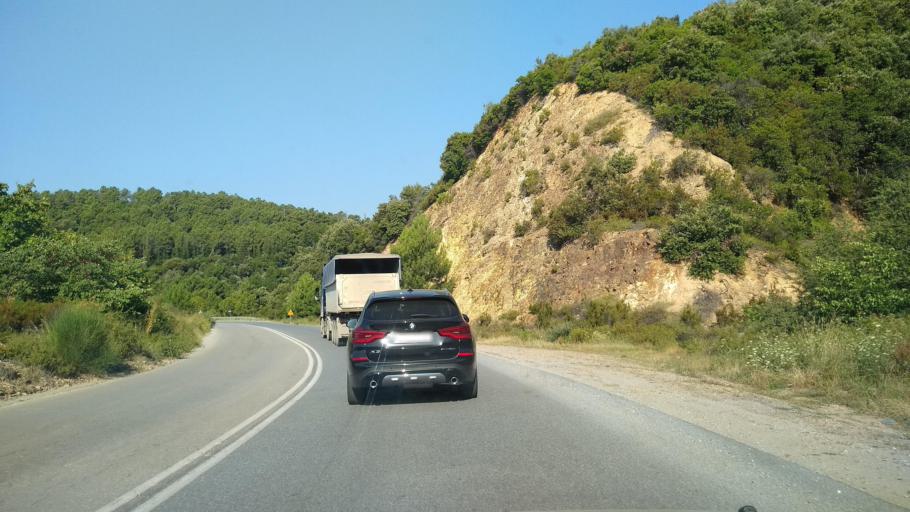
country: GR
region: Central Macedonia
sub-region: Nomos Chalkidikis
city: Stratonion
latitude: 40.5193
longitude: 23.8063
